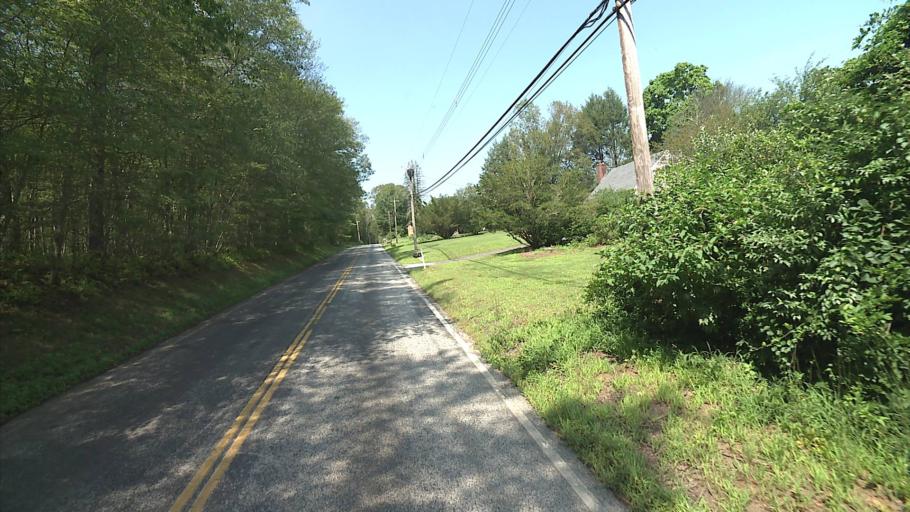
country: US
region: Connecticut
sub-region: New London County
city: Colchester
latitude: 41.5746
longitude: -72.2800
